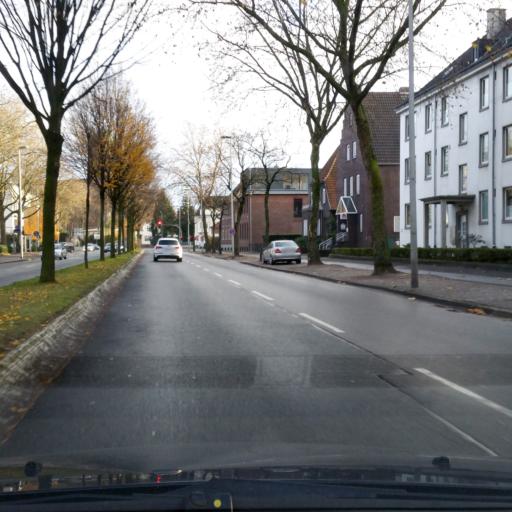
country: DE
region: North Rhine-Westphalia
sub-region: Regierungsbezirk Dusseldorf
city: Bocholt
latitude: 51.8363
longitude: 6.6096
